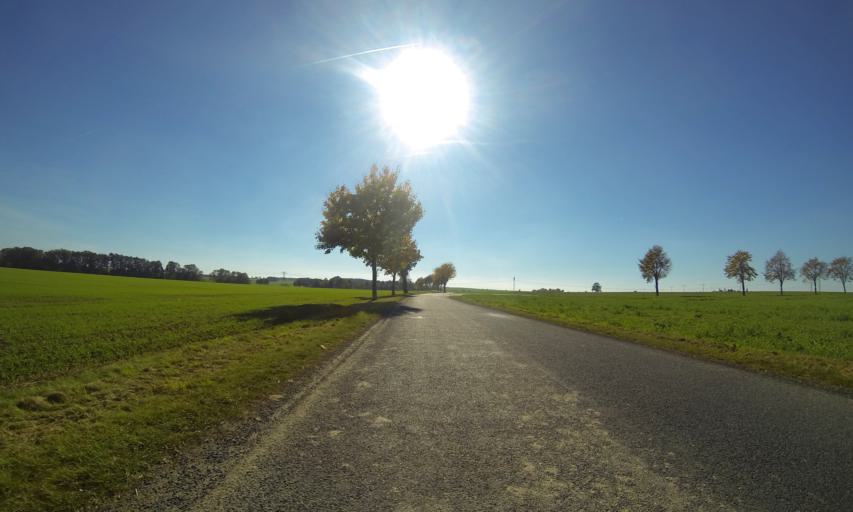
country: DE
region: Saxony
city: Ebersbach
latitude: 51.2258
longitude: 13.5915
